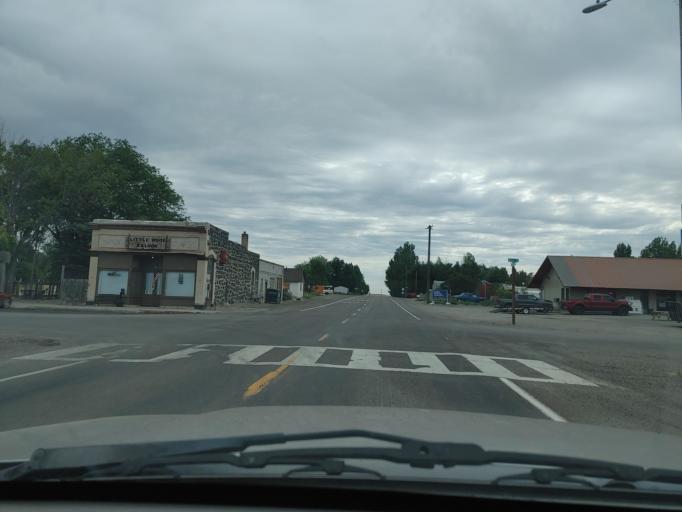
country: US
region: Idaho
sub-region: Lincoln County
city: Shoshone
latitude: 43.0493
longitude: -114.1542
